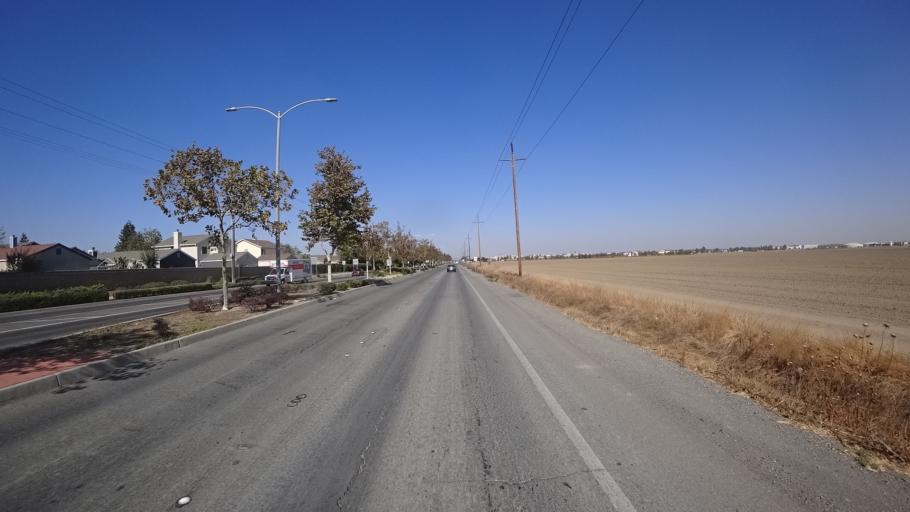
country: US
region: California
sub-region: Yolo County
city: Woodland
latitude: 38.6636
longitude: -121.7286
